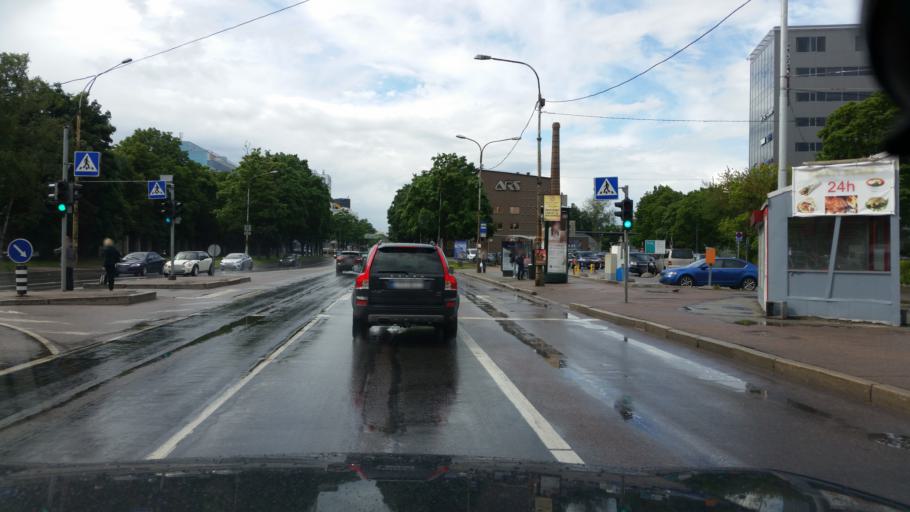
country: EE
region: Harju
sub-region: Tallinna linn
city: Tallinn
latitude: 59.4097
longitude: 24.7361
